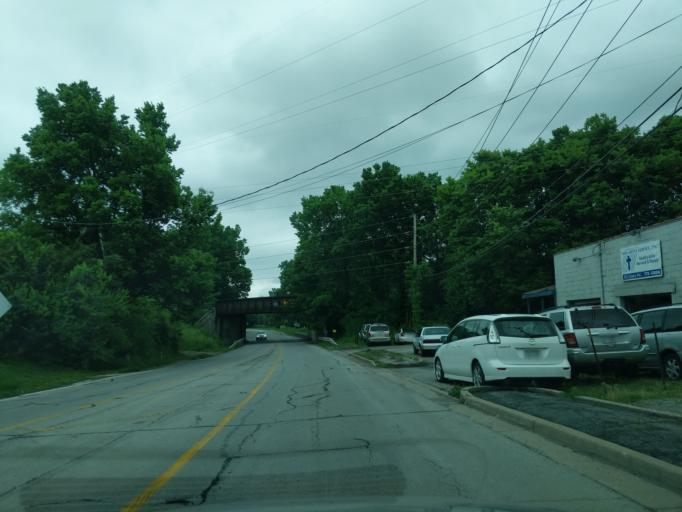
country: US
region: Indiana
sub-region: Hamilton County
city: Noblesville
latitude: 40.0481
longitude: -86.0164
